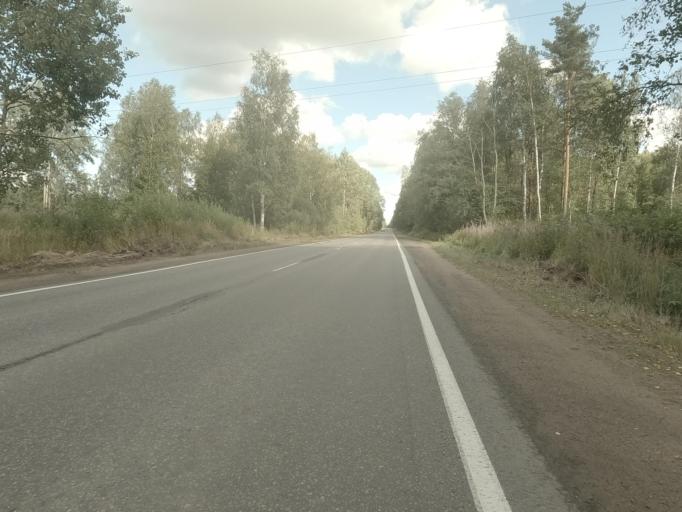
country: RU
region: Leningrad
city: Romanovka
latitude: 60.0214
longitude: 30.7245
